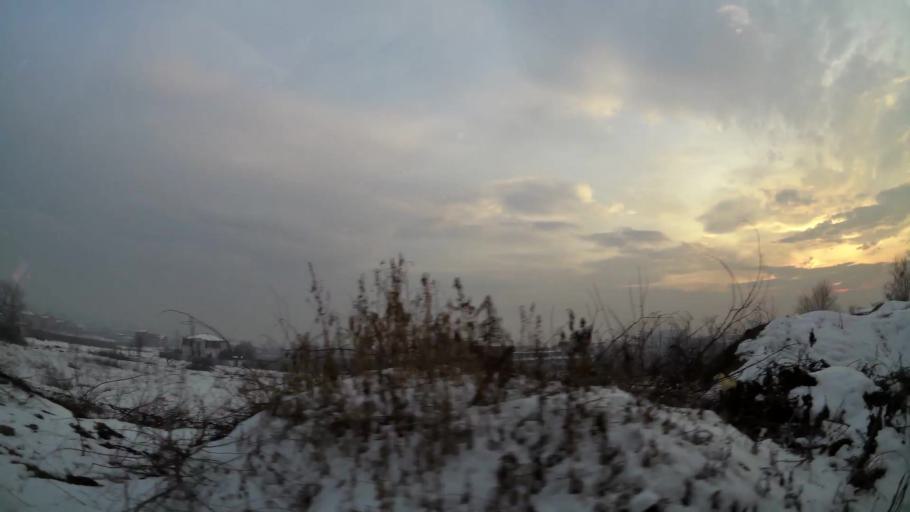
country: MK
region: Suto Orizari
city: Suto Orizare
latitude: 42.0396
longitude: 21.4009
